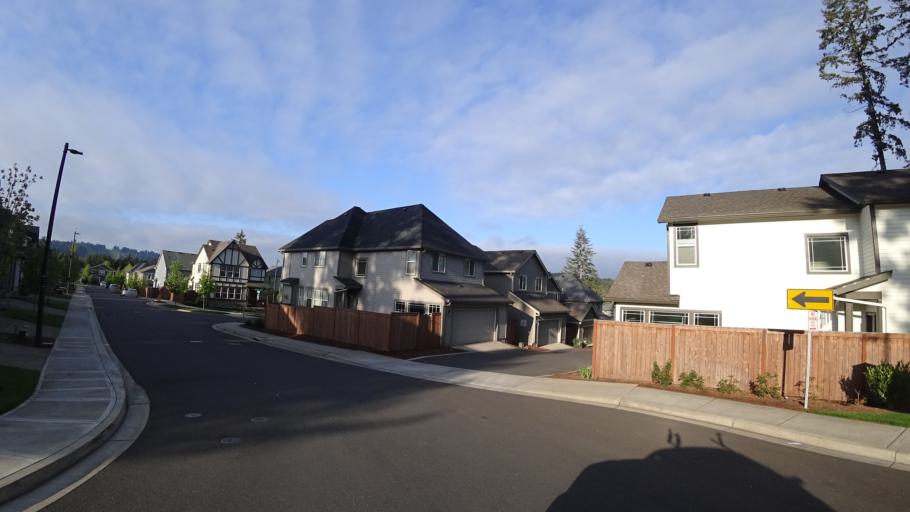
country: US
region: Oregon
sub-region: Washington County
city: Beaverton
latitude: 45.4476
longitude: -122.8238
